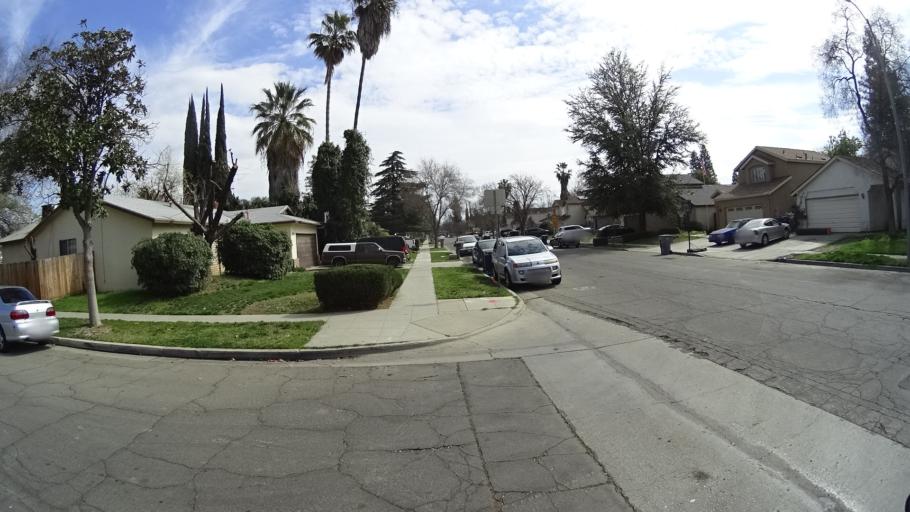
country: US
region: California
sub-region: Fresno County
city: West Park
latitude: 36.8192
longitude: -119.8554
